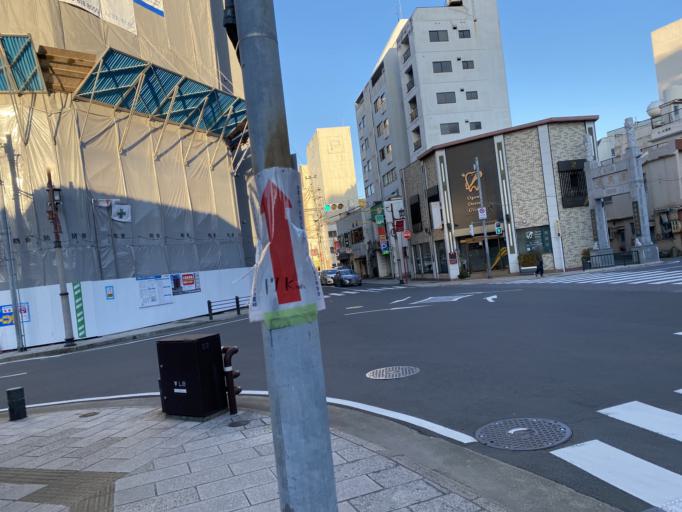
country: JP
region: Nagasaki
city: Nagasaki-shi
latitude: 32.7406
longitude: 129.8751
